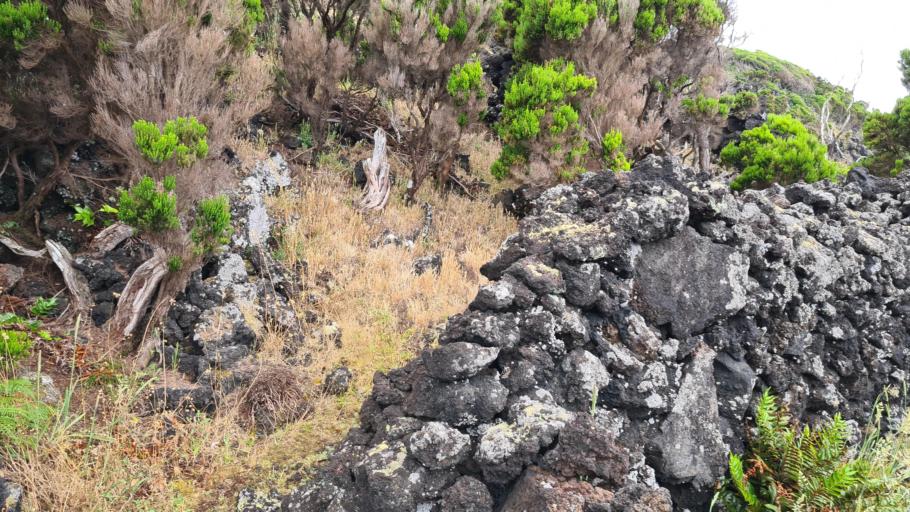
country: PT
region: Azores
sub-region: Sao Roque do Pico
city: Sao Roque do Pico
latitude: 38.5523
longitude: -28.3795
